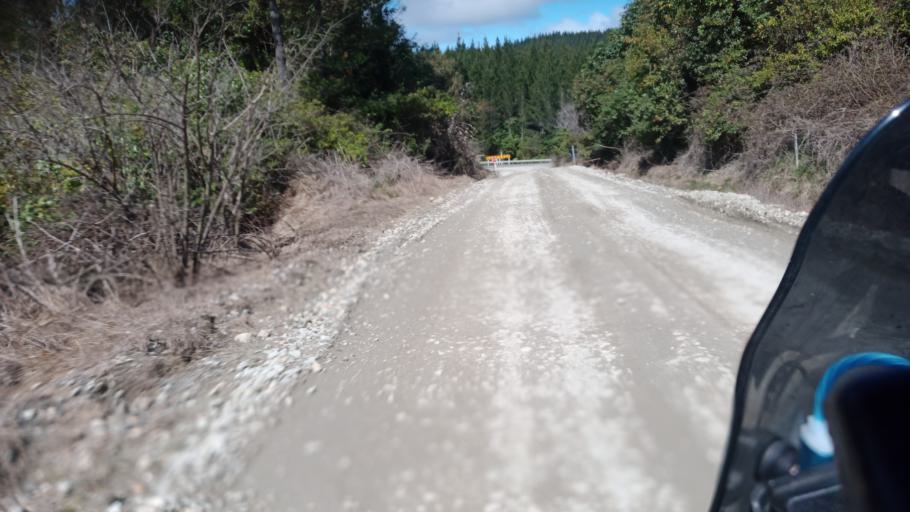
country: NZ
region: Gisborne
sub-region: Gisborne District
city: Gisborne
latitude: -38.9107
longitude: 177.8155
